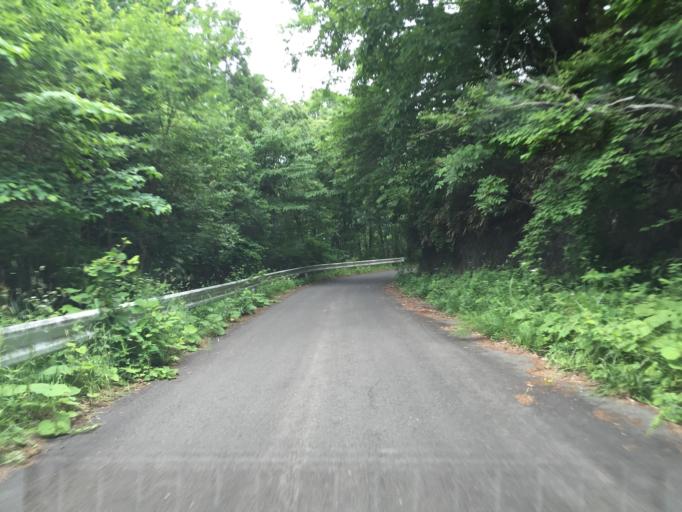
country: JP
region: Fukushima
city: Yanagawamachi-saiwaicho
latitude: 37.7893
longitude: 140.6895
